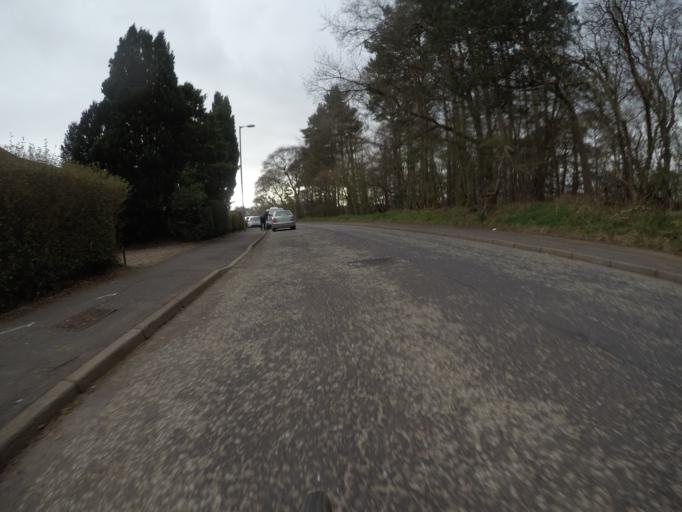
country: GB
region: Scotland
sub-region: East Ayrshire
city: Kilmarnock
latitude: 55.6179
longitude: -4.4838
